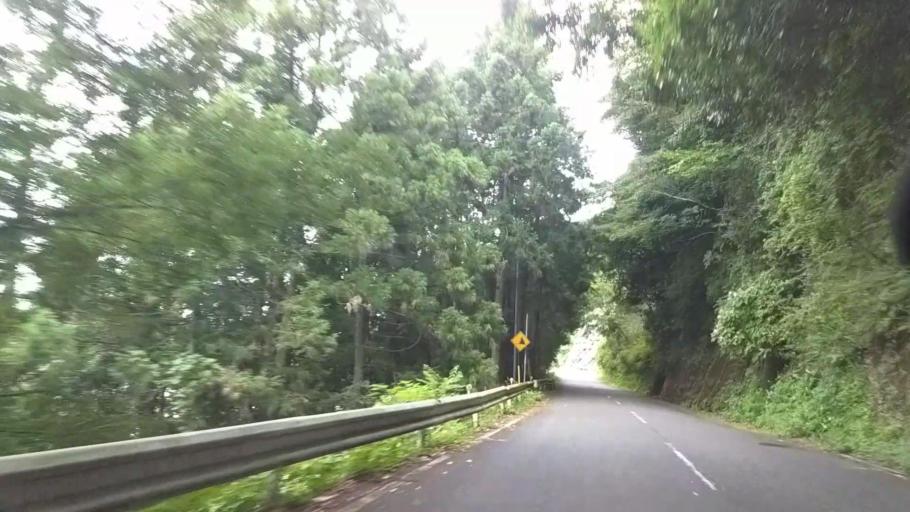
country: JP
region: Shizuoka
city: Fujinomiya
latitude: 35.2077
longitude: 138.5445
